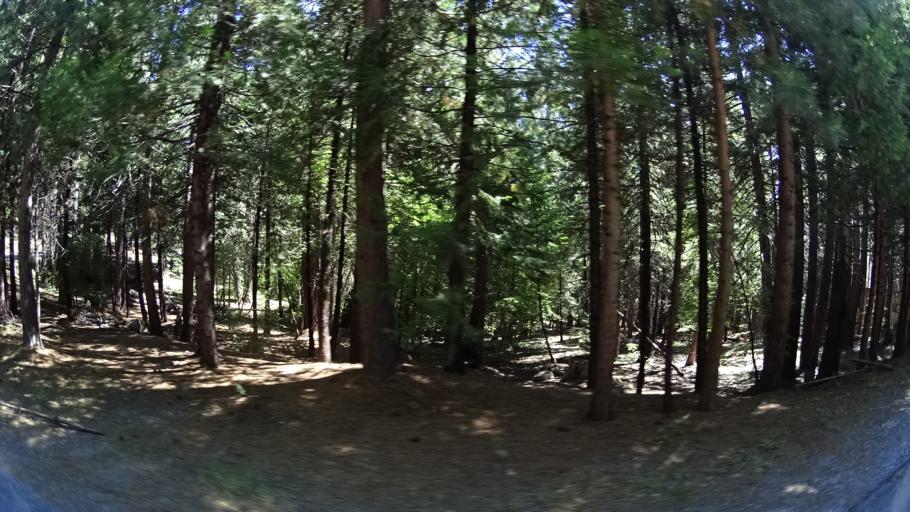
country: US
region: California
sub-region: Calaveras County
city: Arnold
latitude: 38.2860
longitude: -120.2812
